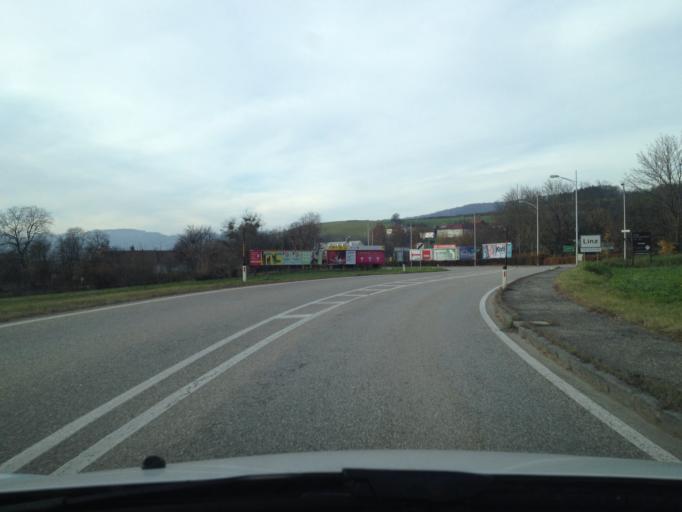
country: AT
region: Upper Austria
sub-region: Politischer Bezirk Urfahr-Umgebung
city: Altenberg bei Linz
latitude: 48.3269
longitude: 14.3365
